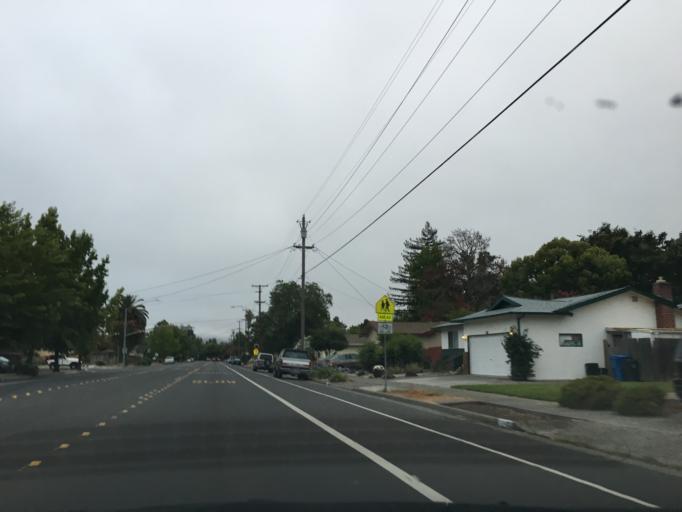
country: US
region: California
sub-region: Sonoma County
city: Santa Rosa
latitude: 38.4697
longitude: -122.6767
